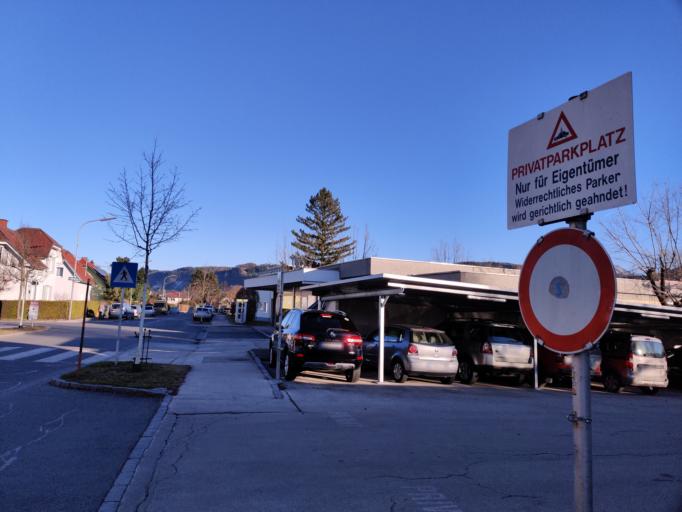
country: AT
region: Carinthia
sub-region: Klagenfurt am Woerthersee
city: Klagenfurt am Woerthersee
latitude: 46.6043
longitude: 14.2927
